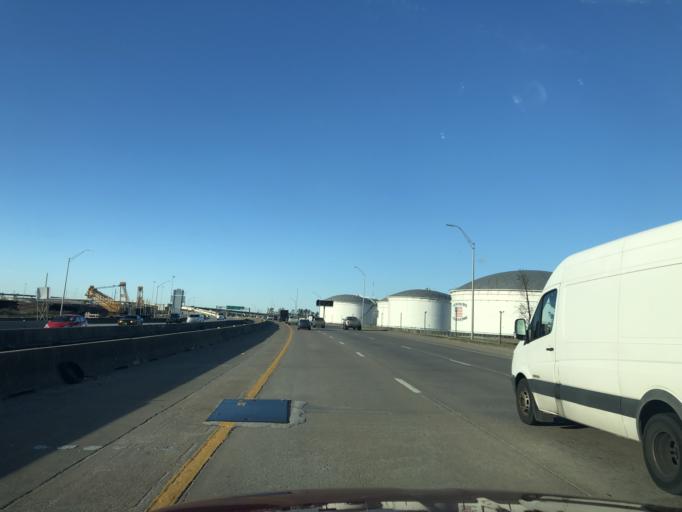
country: US
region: Texas
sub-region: Harris County
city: Cloverleaf
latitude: 29.7604
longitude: -95.1462
